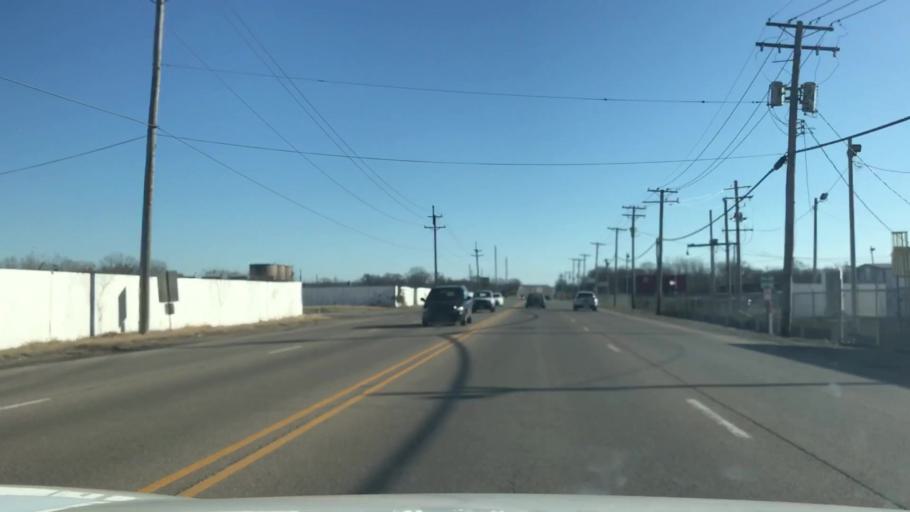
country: US
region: Illinois
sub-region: Saint Clair County
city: Alorton
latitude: 38.5983
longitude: -90.1260
